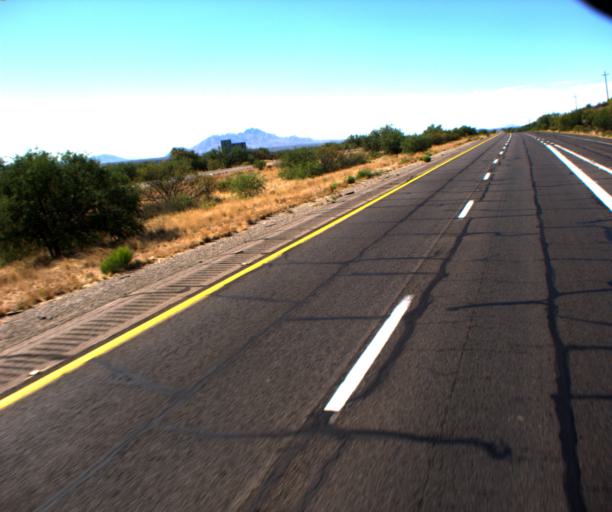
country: US
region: Arizona
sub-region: Pima County
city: Arivaca Junction
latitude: 31.6726
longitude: -111.0637
